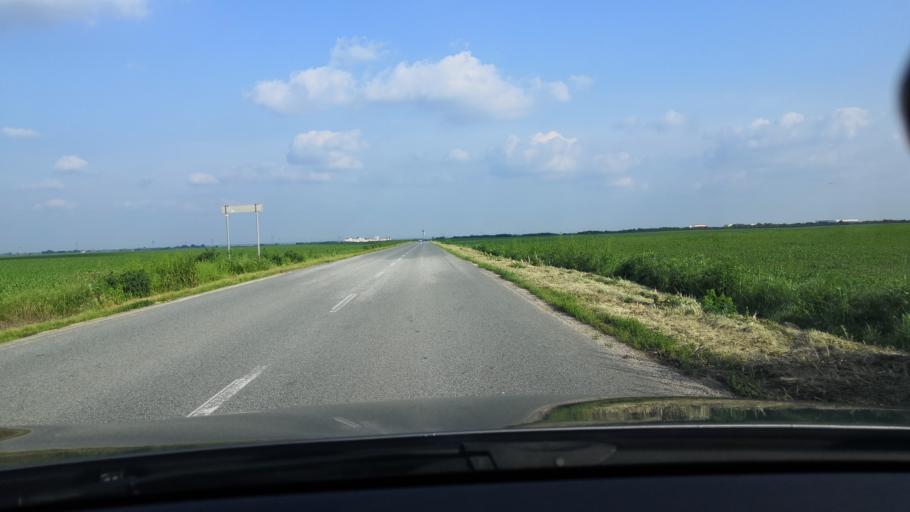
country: RS
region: Autonomna Pokrajina Vojvodina
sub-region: Sremski Okrug
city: Ingija
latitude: 45.0835
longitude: 20.1140
